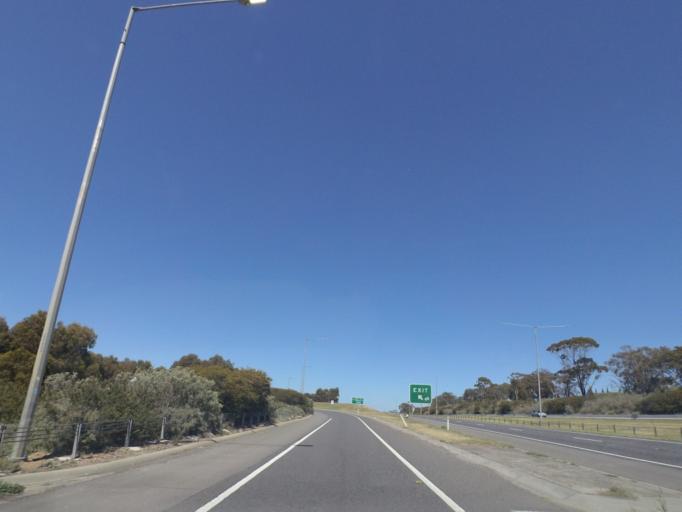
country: AU
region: Victoria
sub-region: Hume
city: Craigieburn
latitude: -37.5674
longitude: 144.9415
